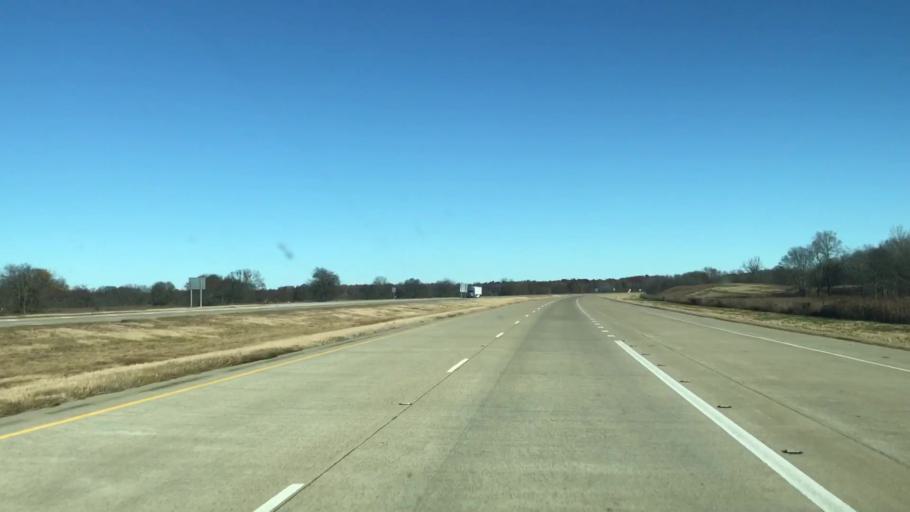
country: US
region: Louisiana
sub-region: Caddo Parish
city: Oil City
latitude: 32.7728
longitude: -93.8891
